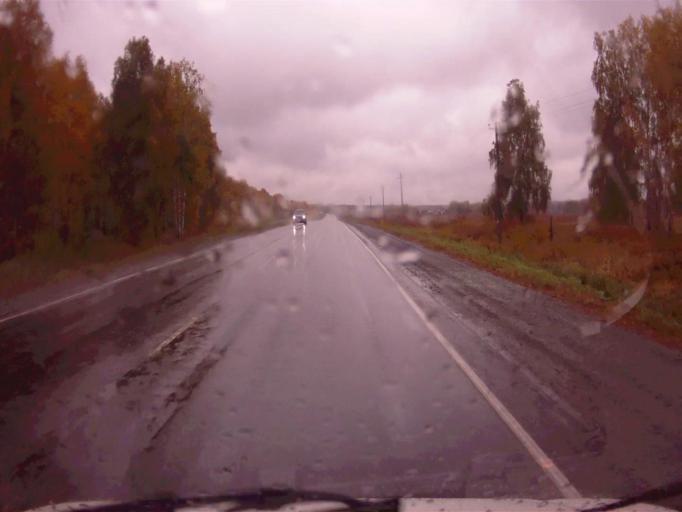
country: RU
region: Chelyabinsk
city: Argayash
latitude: 55.4026
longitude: 61.0682
